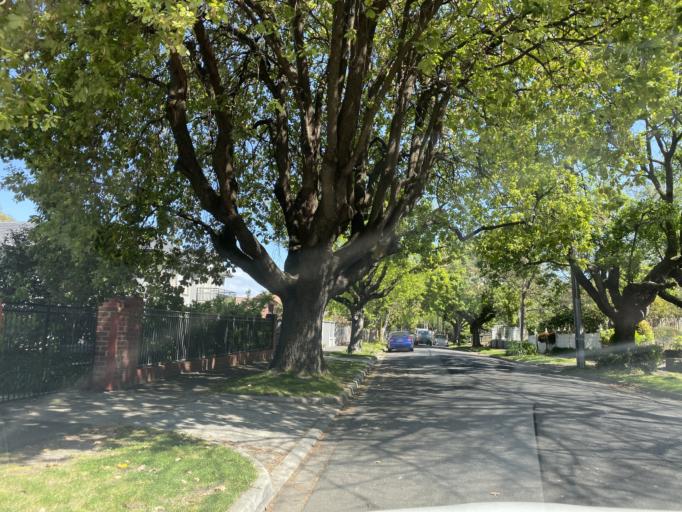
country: AU
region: Victoria
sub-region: Boroondara
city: Camberwell
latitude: -37.8459
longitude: 145.0655
